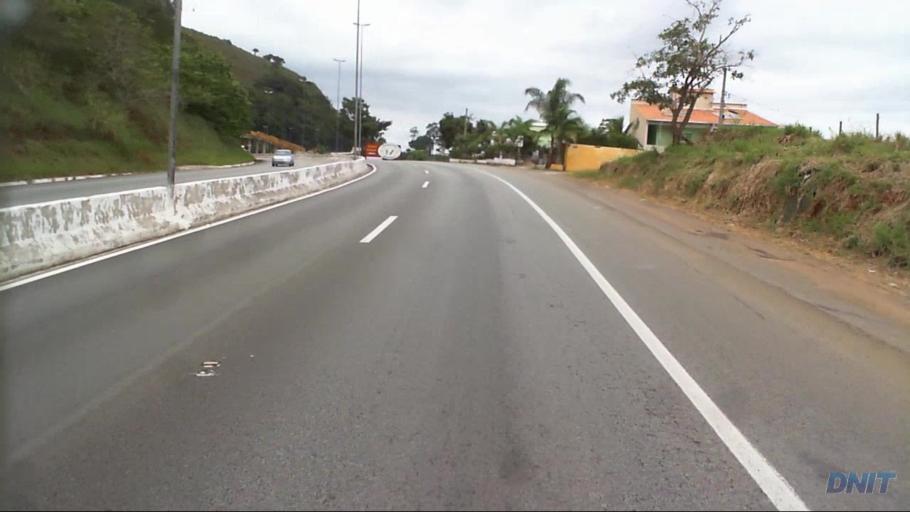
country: BR
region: Minas Gerais
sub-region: Nova Era
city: Nova Era
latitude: -19.7617
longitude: -43.0453
